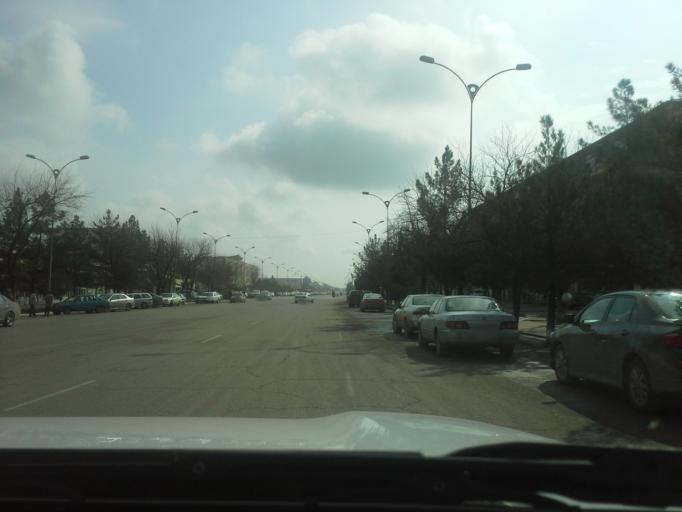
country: TM
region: Mary
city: Mary
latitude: 37.5961
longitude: 61.8303
